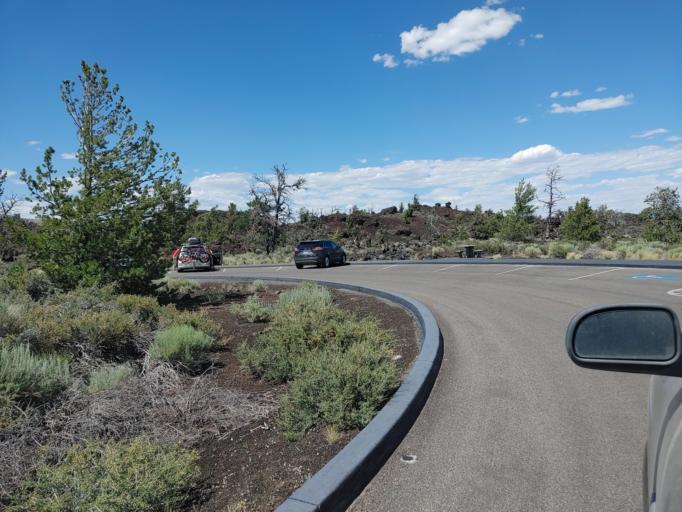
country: US
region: Idaho
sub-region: Butte County
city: Arco
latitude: 43.4515
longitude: -113.5385
